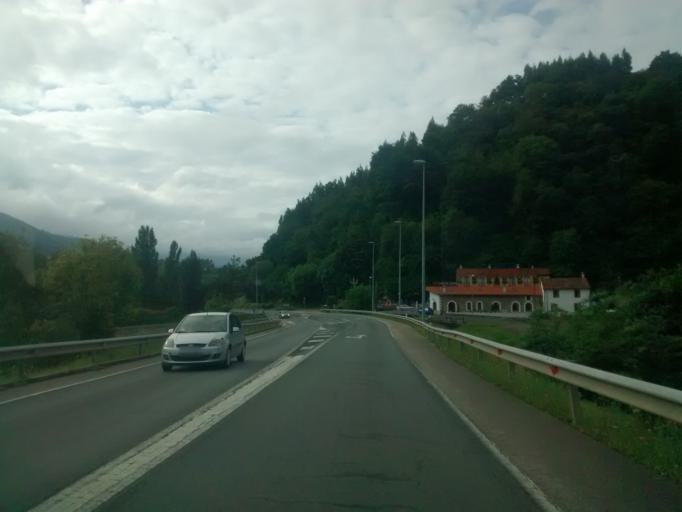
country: ES
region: Cantabria
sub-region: Provincia de Cantabria
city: Santiurde de Toranzo
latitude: 43.2370
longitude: -3.9485
